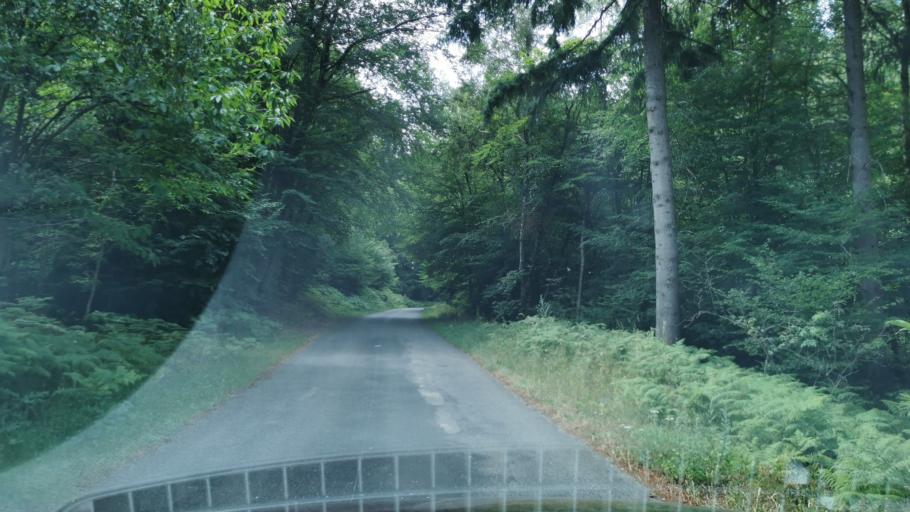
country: FR
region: Bourgogne
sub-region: Departement de Saone-et-Loire
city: Marmagne
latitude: 46.8081
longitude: 4.2875
